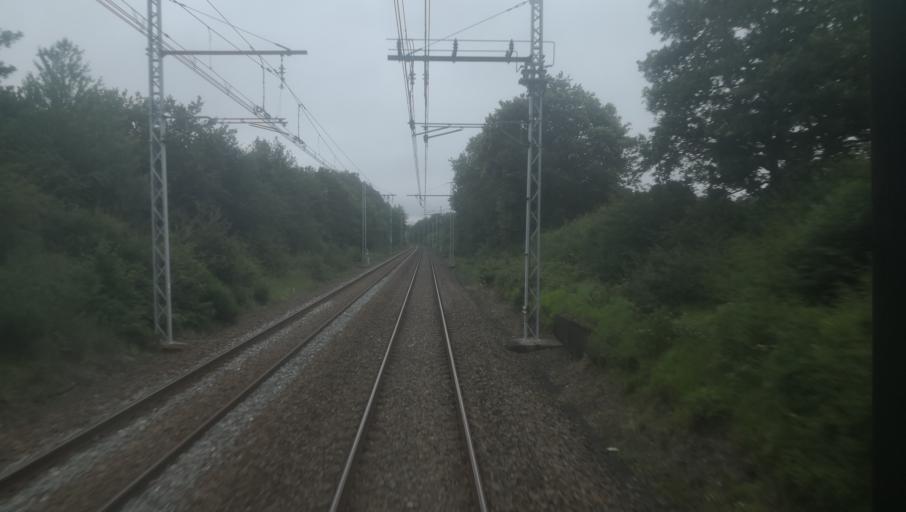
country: FR
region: Centre
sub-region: Departement de l'Indre
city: Luant
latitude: 46.6856
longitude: 1.5561
